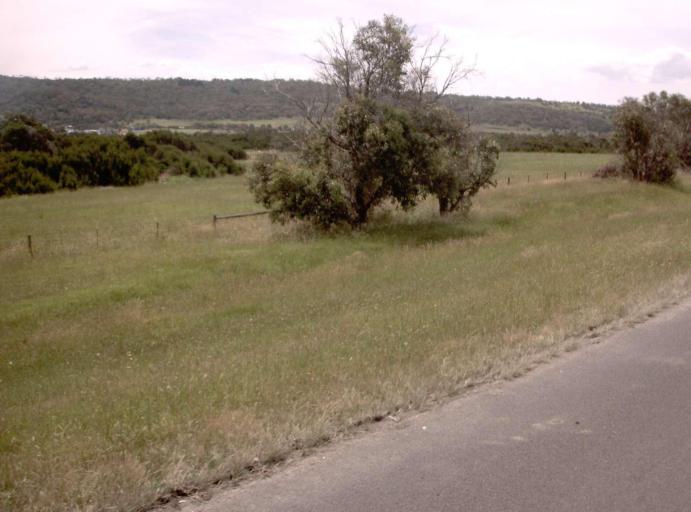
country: AU
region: Victoria
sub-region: Mornington Peninsula
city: Safety Beach
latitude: -38.3145
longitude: 145.0143
